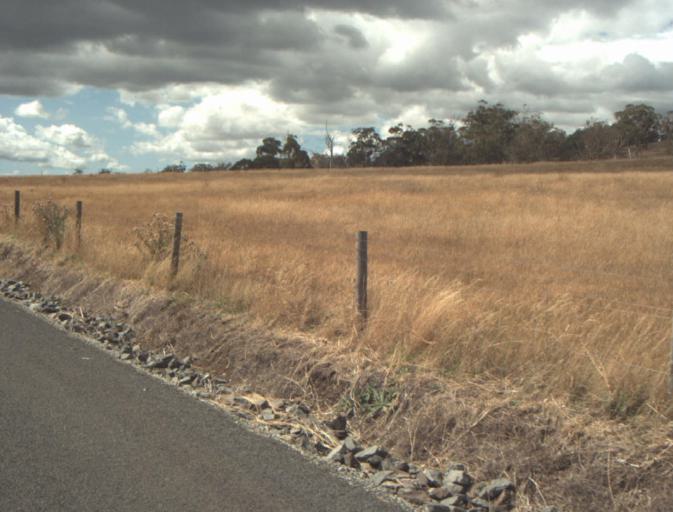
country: AU
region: Tasmania
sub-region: Launceston
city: Mayfield
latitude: -41.3100
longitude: 146.9952
